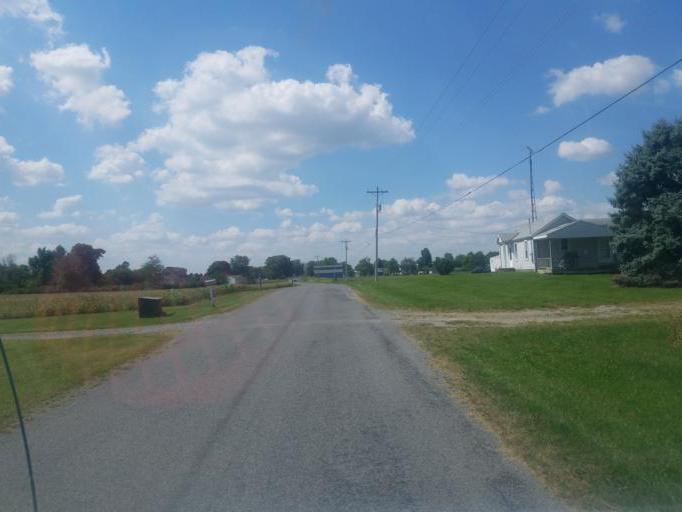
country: US
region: Ohio
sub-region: Hardin County
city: Ada
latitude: 40.6542
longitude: -83.8881
